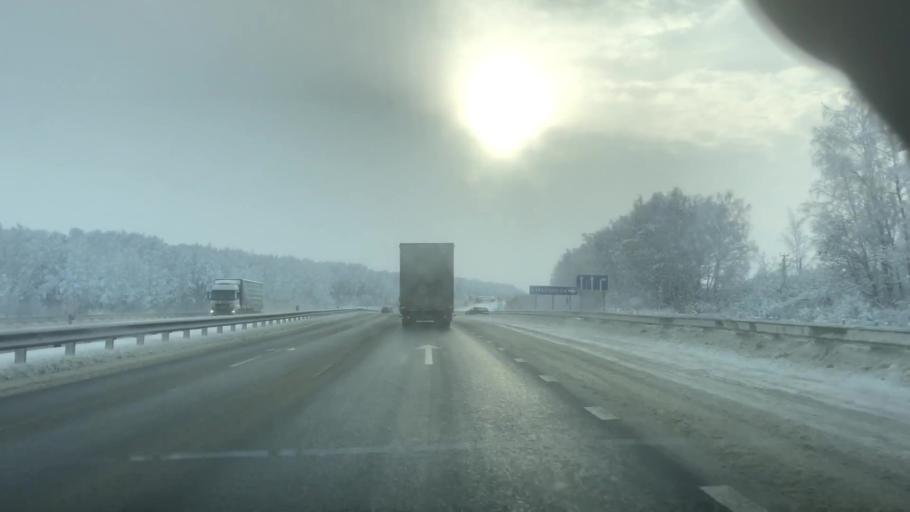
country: RU
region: Tula
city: Venev
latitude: 54.5177
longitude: 38.1699
